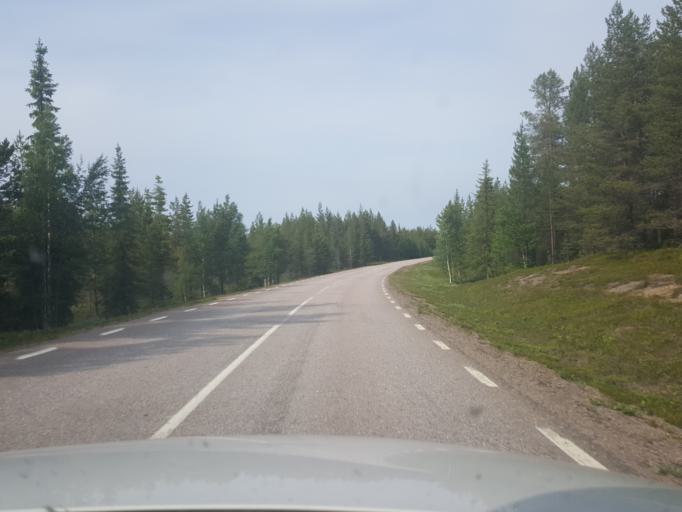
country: SE
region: Norrbotten
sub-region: Arjeplogs Kommun
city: Arjeplog
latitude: 65.8261
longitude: 18.0079
